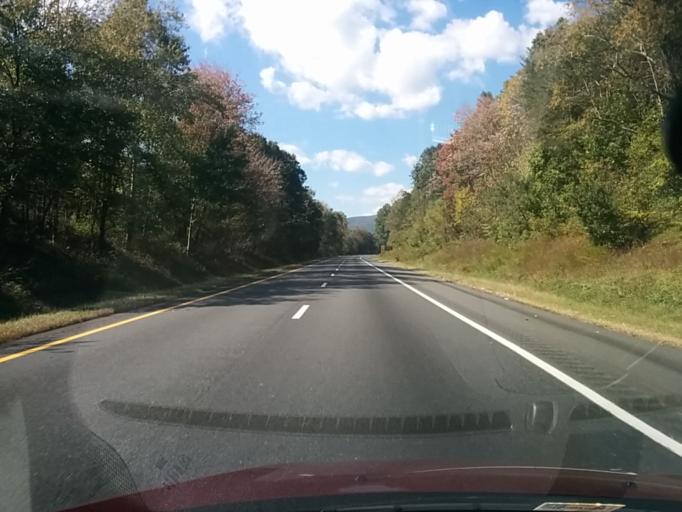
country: US
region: Virginia
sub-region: Albemarle County
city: Crozet
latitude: 38.0399
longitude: -78.7127
